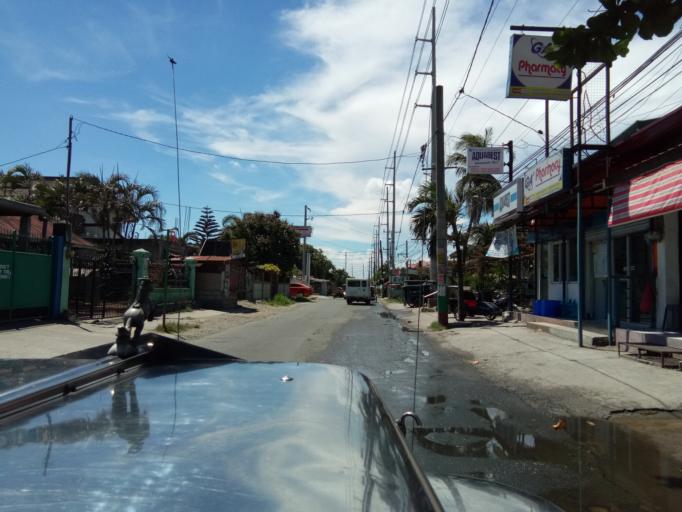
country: PH
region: Calabarzon
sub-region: Province of Cavite
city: Pasong Kawayan Primero
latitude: 14.3625
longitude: 120.8953
